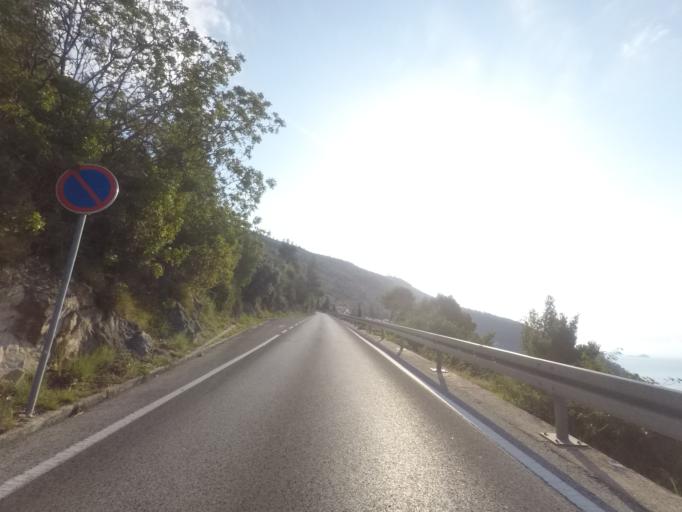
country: HR
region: Dubrovacko-Neretvanska
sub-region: Grad Dubrovnik
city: Dubrovnik
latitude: 42.6408
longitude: 18.1234
